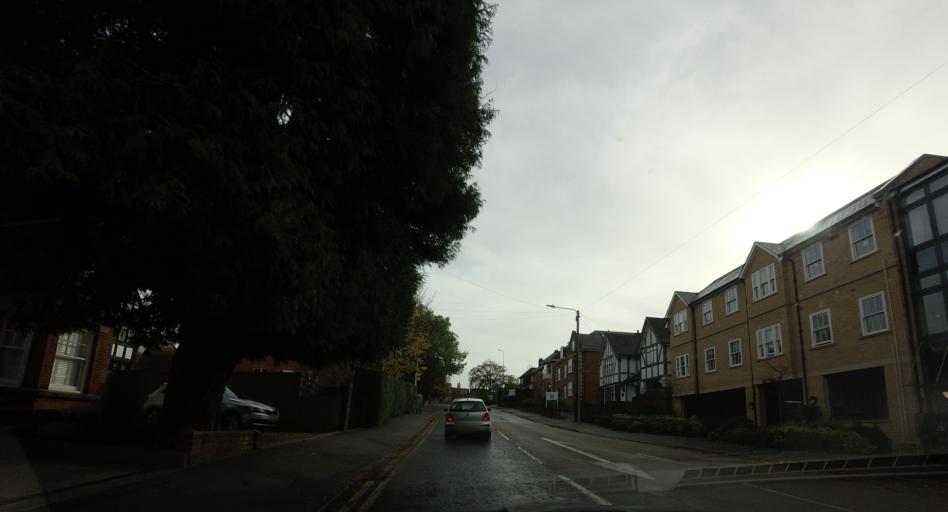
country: GB
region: England
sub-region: Kent
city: Sevenoaks
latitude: 51.2734
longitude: 0.1902
